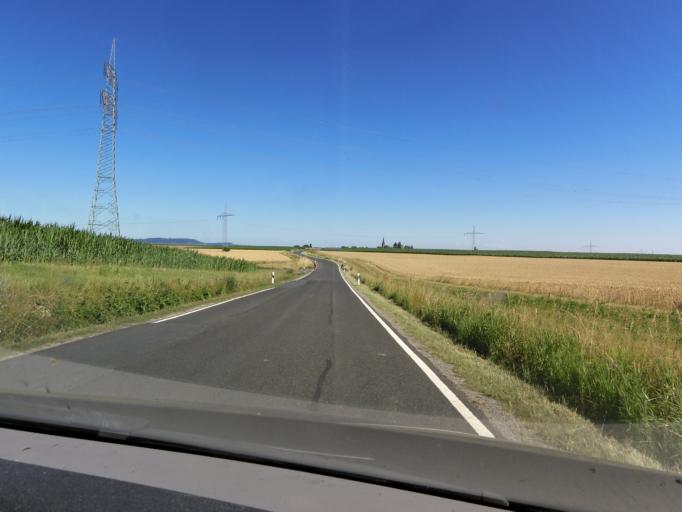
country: DE
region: Bavaria
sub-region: Regierungsbezirk Unterfranken
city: Theilheim
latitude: 49.7503
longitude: 10.0517
